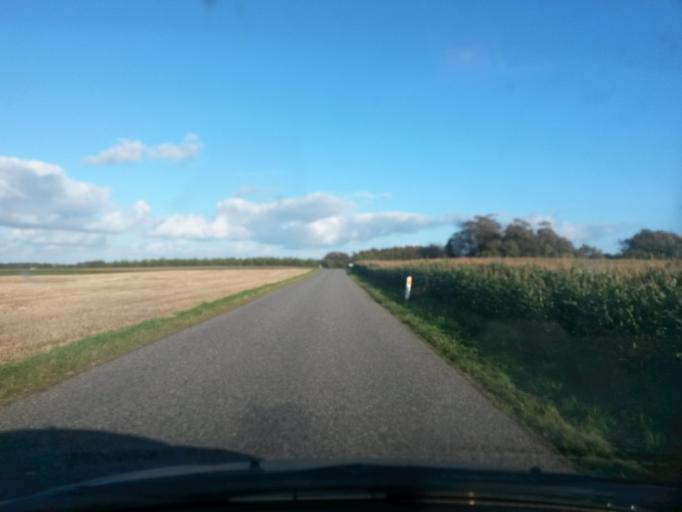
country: DK
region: Central Jutland
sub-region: Silkeborg Kommune
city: Kjellerup
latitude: 56.3376
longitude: 9.4150
